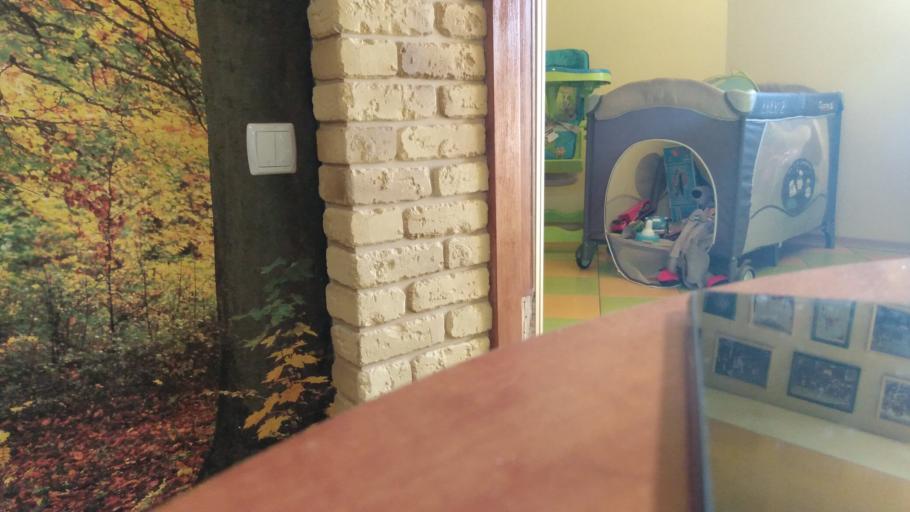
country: RU
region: Tverskaya
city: Bologoye
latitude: 57.8992
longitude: 34.2574
